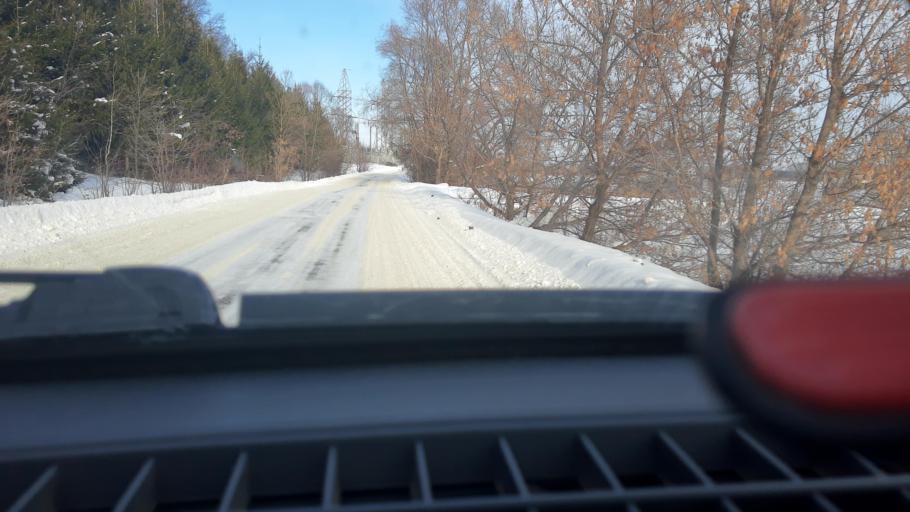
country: RU
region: Bashkortostan
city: Ufa
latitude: 54.5290
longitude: 55.9115
